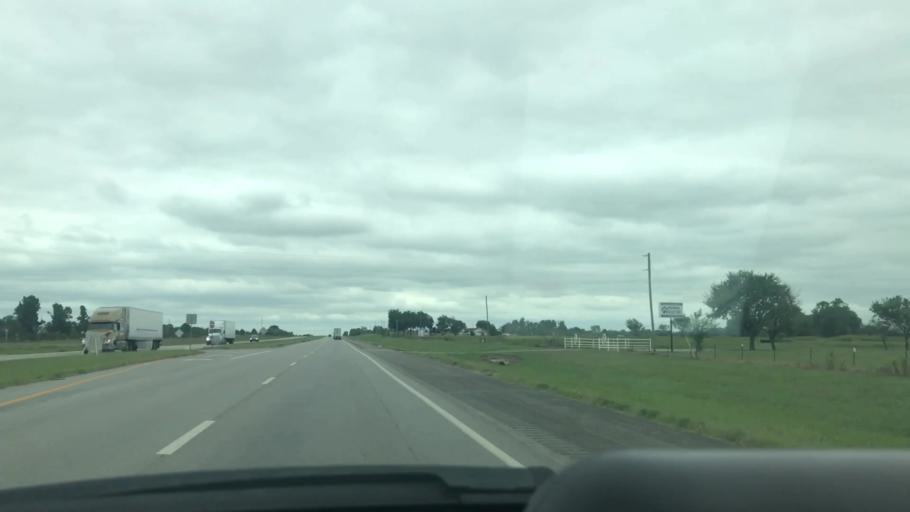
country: US
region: Oklahoma
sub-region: Mayes County
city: Pryor
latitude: 36.3250
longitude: -95.3122
